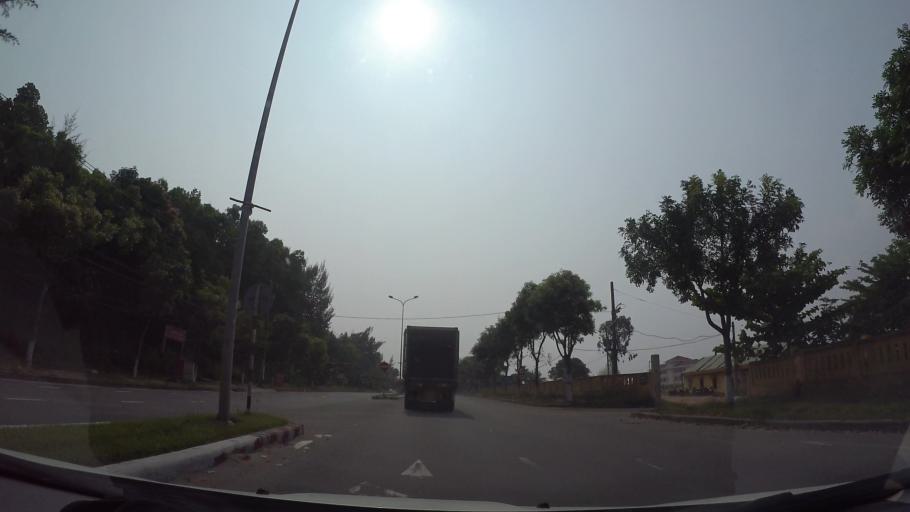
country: VN
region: Da Nang
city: Da Nang
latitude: 16.1156
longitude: 108.2337
